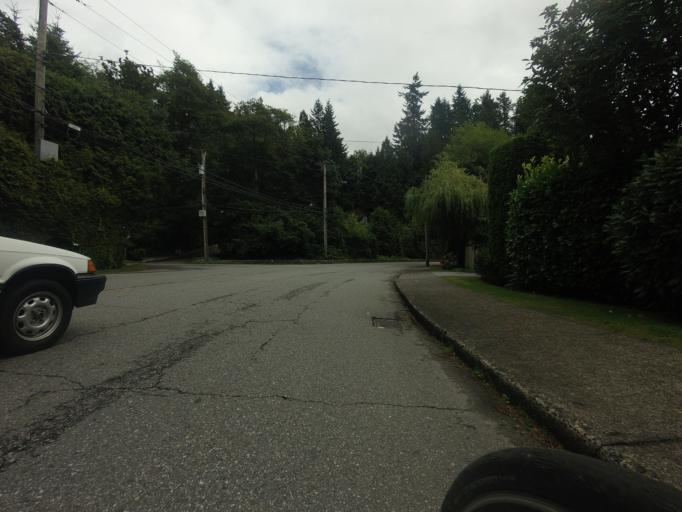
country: CA
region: British Columbia
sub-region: Greater Vancouver Regional District
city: Bowen Island
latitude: 49.3562
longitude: -123.2630
